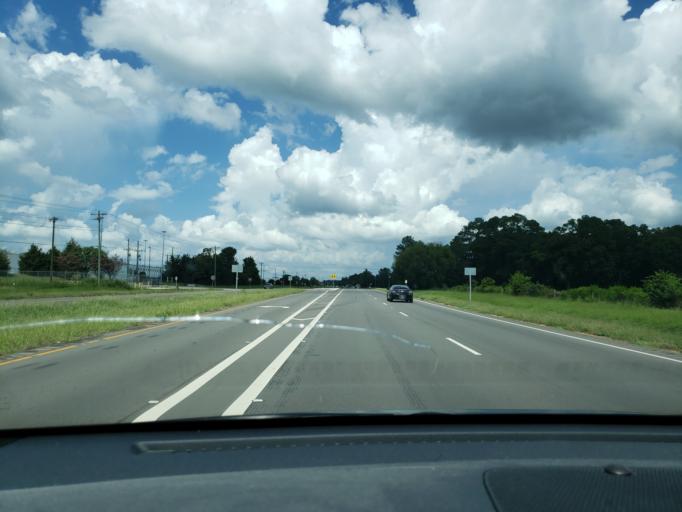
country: US
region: North Carolina
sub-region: Robeson County
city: Saint Pauls
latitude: 34.7442
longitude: -78.8018
